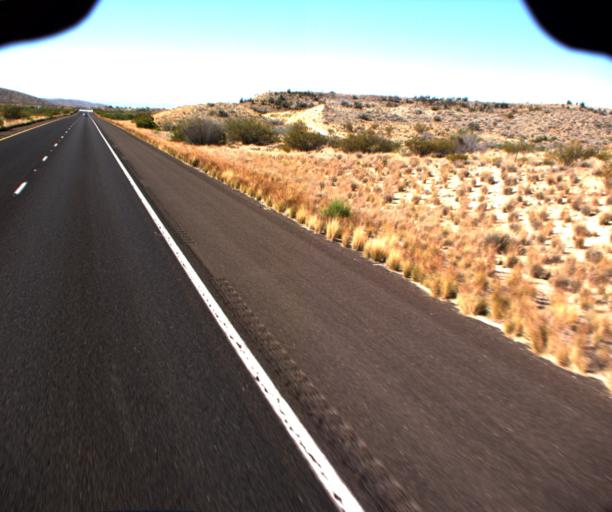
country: US
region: Arizona
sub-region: Mohave County
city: Kingman
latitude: 35.0432
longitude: -113.6653
